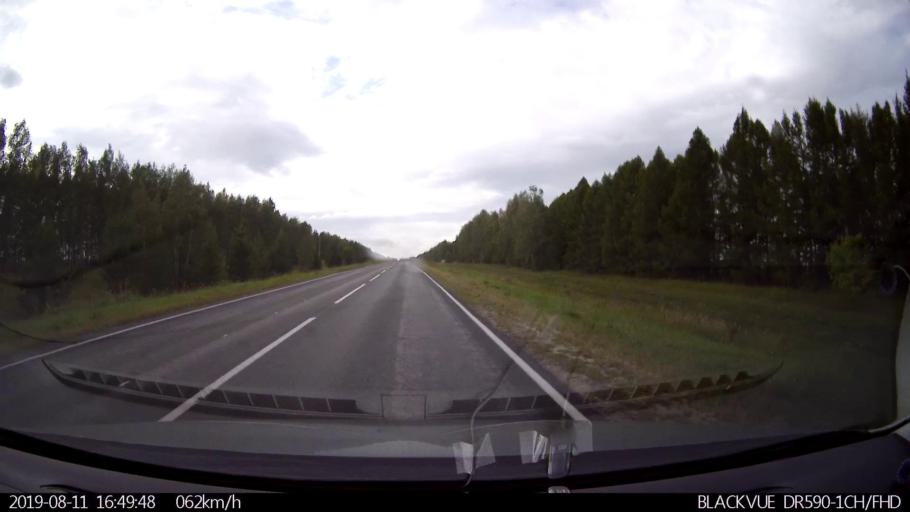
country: RU
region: Ulyanovsk
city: Mayna
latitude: 54.2236
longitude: 47.6943
